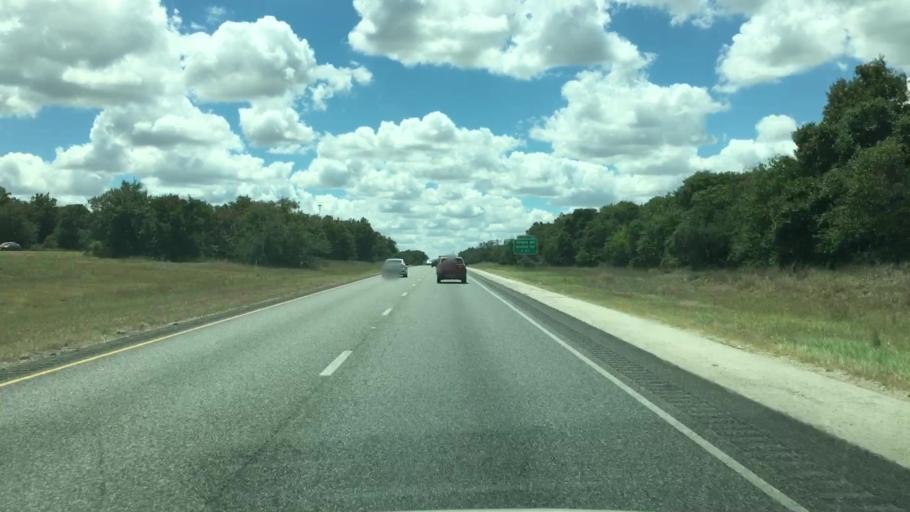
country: US
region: Texas
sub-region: Bexar County
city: Elmendorf
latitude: 29.1981
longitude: -98.4207
